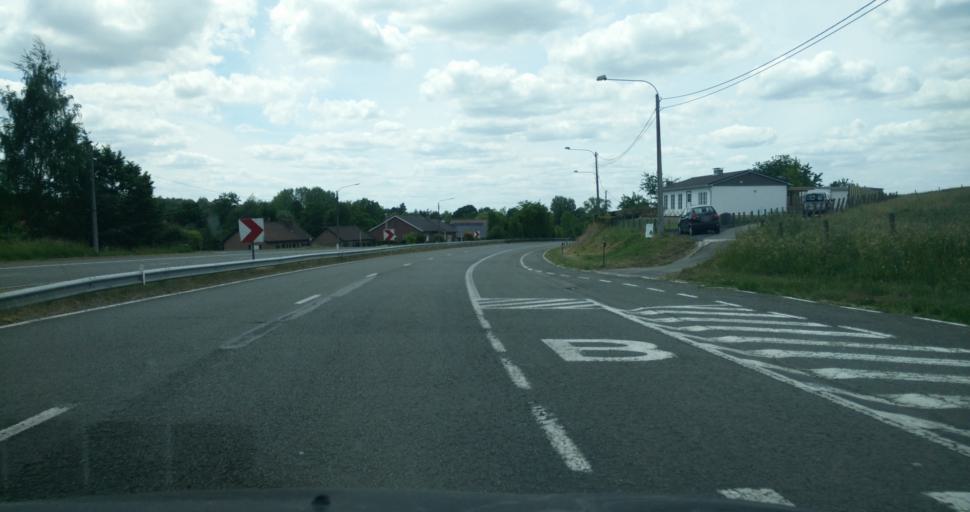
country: BE
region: Wallonia
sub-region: Province du Hainaut
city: Ellezelles
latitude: 50.7544
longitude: 3.6662
